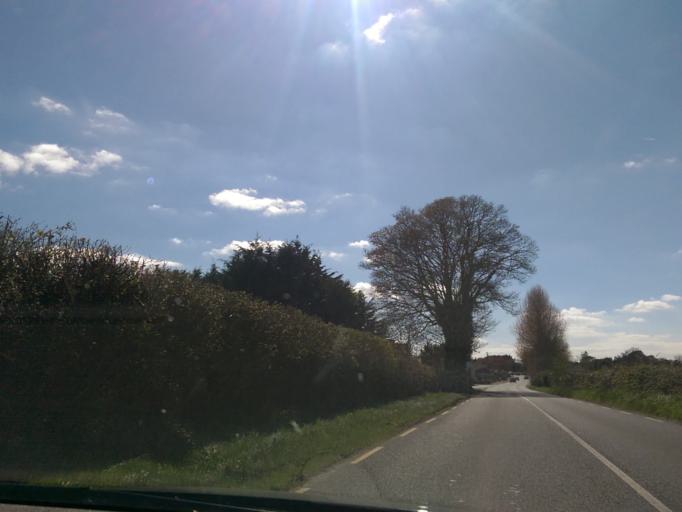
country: IE
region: Leinster
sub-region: Laois
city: Stradbally
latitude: 53.0137
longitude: -7.1368
